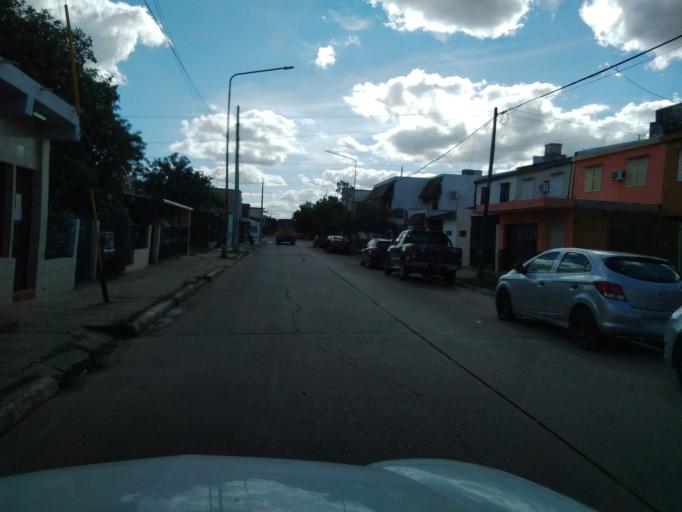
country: AR
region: Corrientes
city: Corrientes
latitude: -27.4965
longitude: -58.8314
